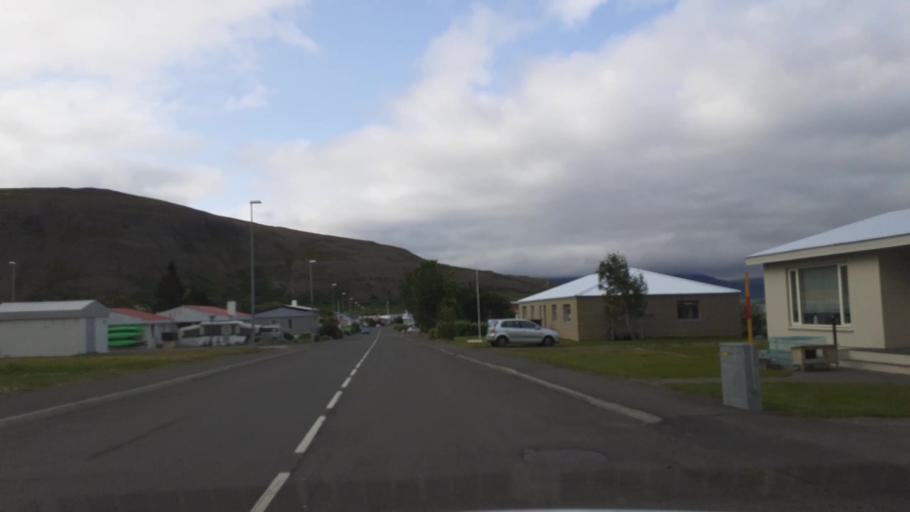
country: IS
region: Northeast
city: Akureyri
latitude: 65.9510
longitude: -18.1794
